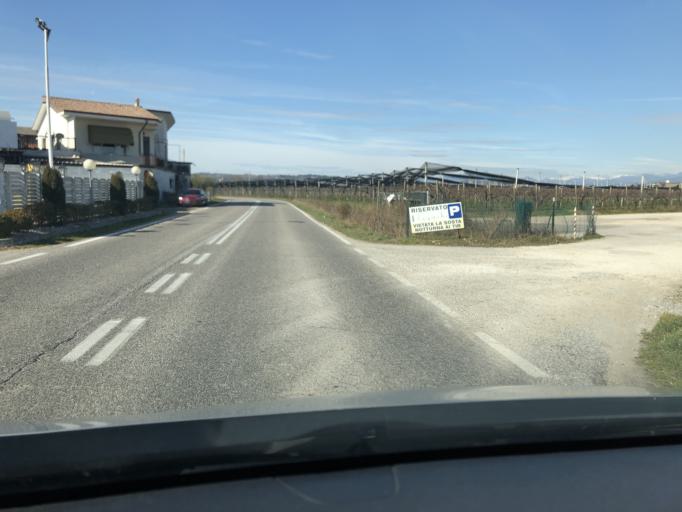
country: IT
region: Veneto
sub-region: Provincia di Verona
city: Sona
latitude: 45.4465
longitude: 10.8559
